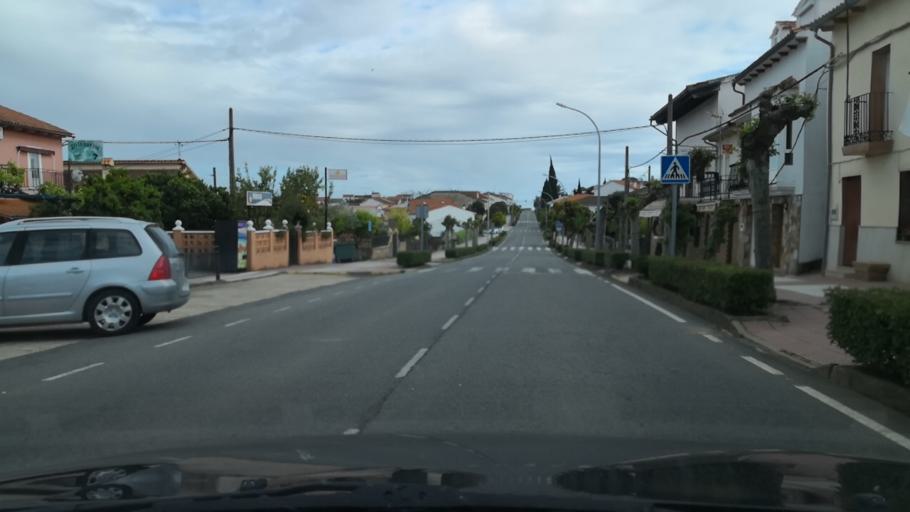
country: ES
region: Extremadura
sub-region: Provincia de Caceres
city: Perales del Puerto
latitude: 40.1586
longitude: -6.6824
